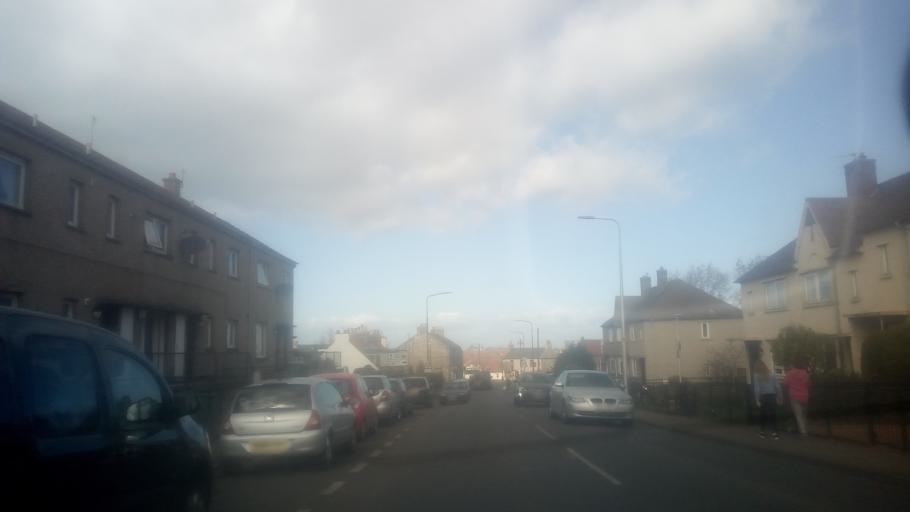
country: GB
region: Scotland
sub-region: East Lothian
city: Tranent
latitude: 55.9418
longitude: -2.9485
